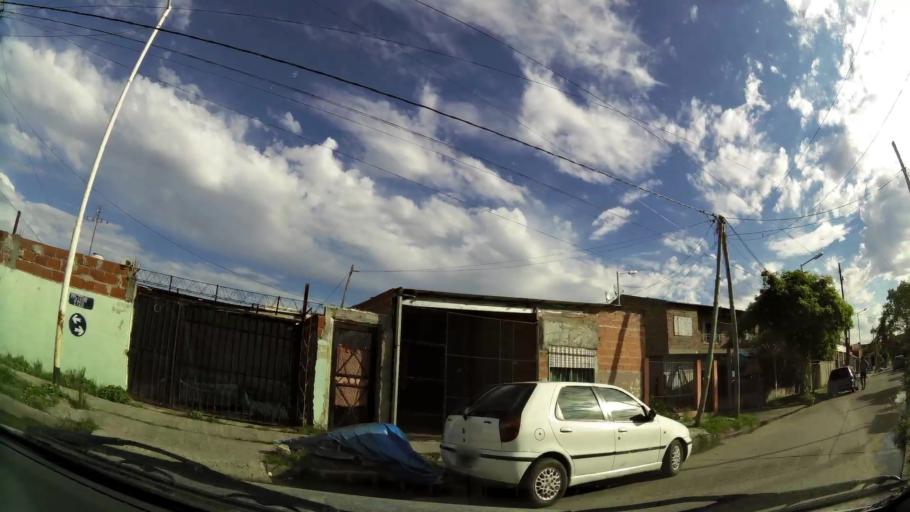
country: AR
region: Buenos Aires
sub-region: Partido de Lanus
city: Lanus
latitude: -34.7021
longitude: -58.3568
